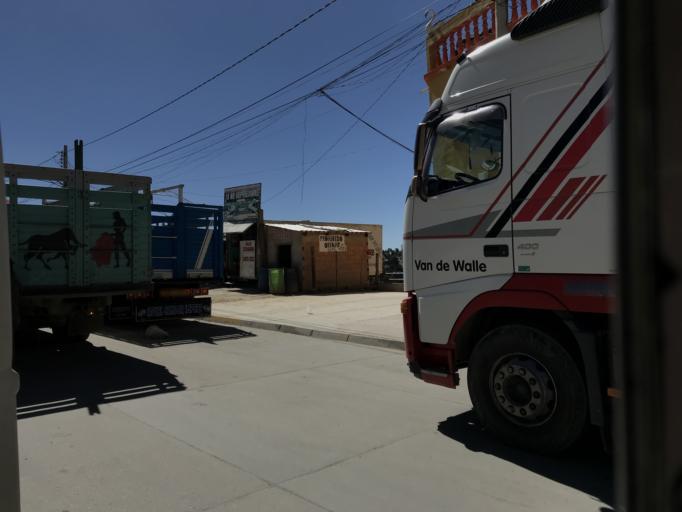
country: BO
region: Chuquisaca
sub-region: Provincia Oropeza
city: Huata
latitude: -19.0186
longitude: -65.2497
